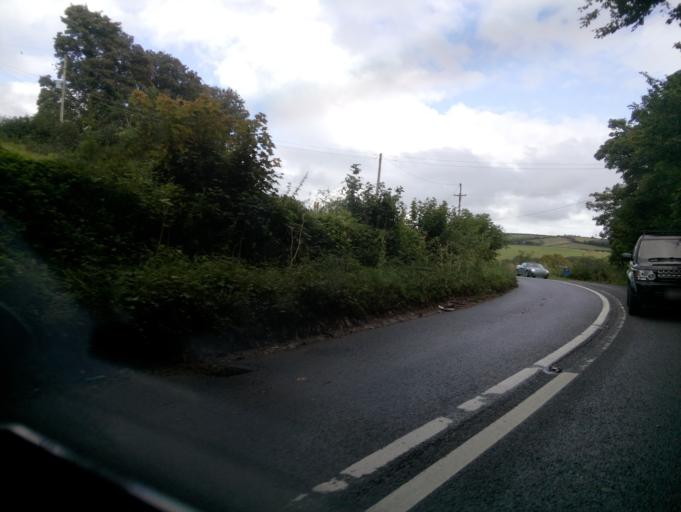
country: GB
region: England
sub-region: Devon
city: Modbury
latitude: 50.3496
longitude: -3.9209
